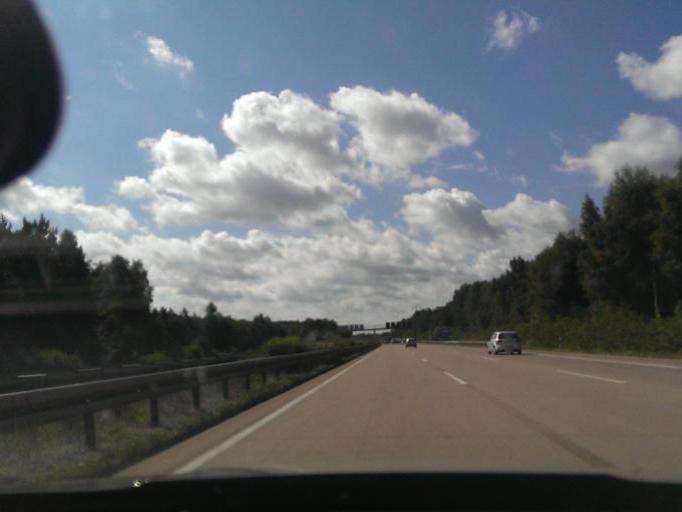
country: DE
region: Lower Saxony
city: Isernhagen Farster Bauerschaft
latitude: 52.5124
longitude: 9.8203
